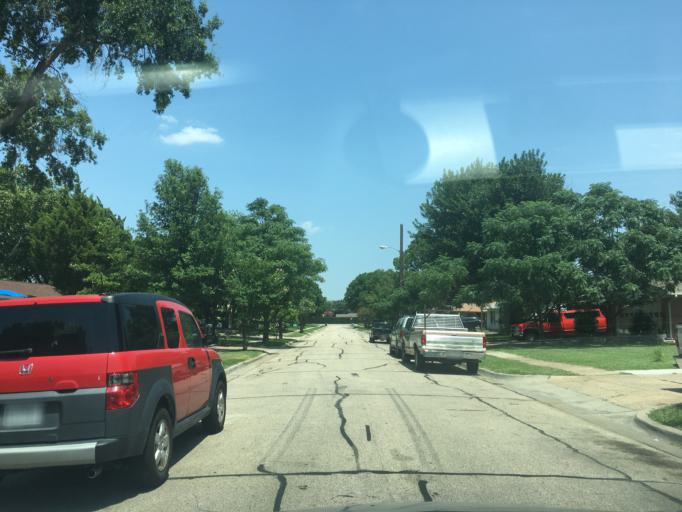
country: US
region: Texas
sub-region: Dallas County
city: Carrollton
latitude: 32.9380
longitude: -96.8777
